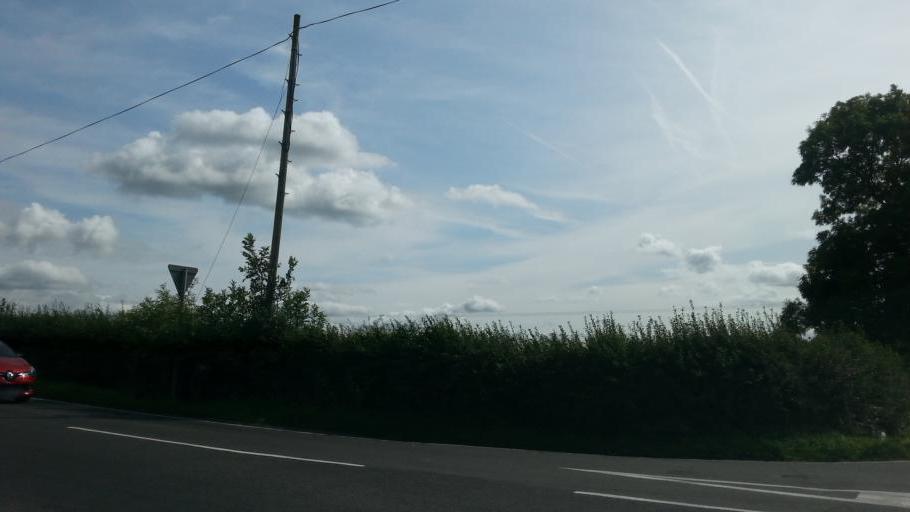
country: GB
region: England
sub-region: Leicestershire
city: Wigston Magna
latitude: 52.5106
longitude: -1.0764
